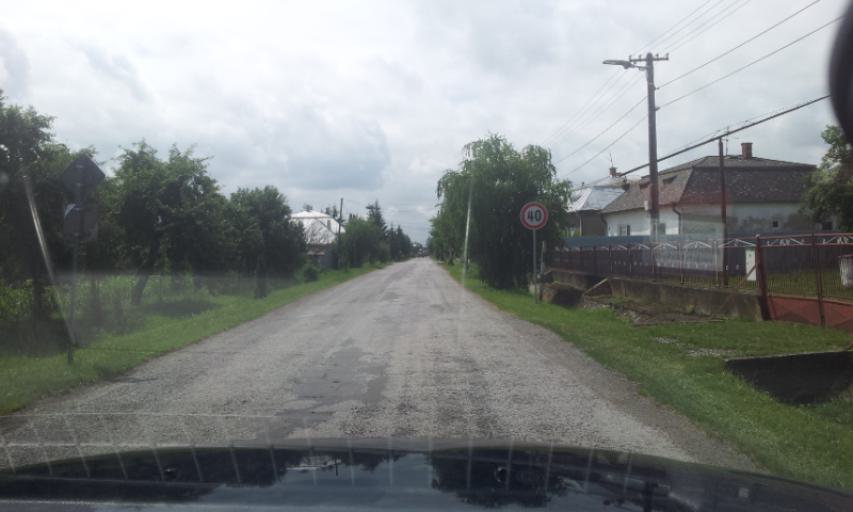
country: SK
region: Kosicky
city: Michalovce
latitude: 48.6458
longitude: 22.0005
